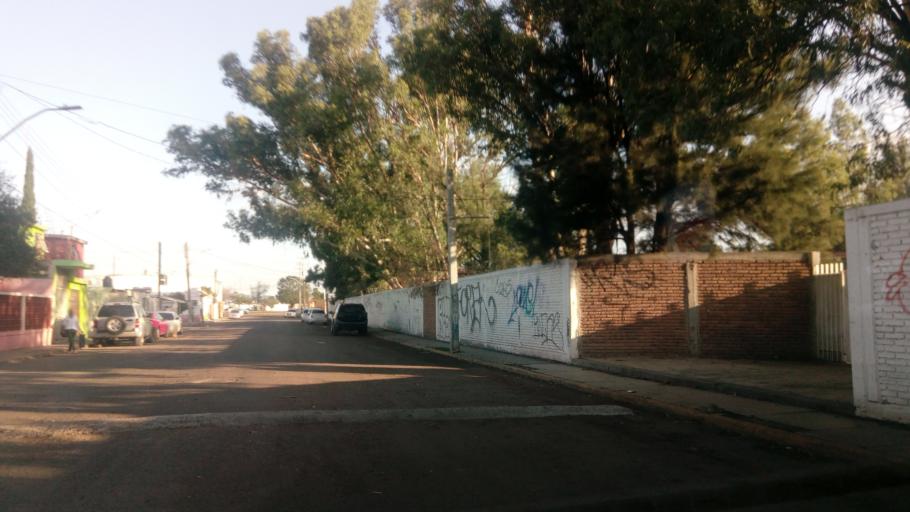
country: MX
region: Durango
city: Victoria de Durango
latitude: 24.0484
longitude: -104.6197
